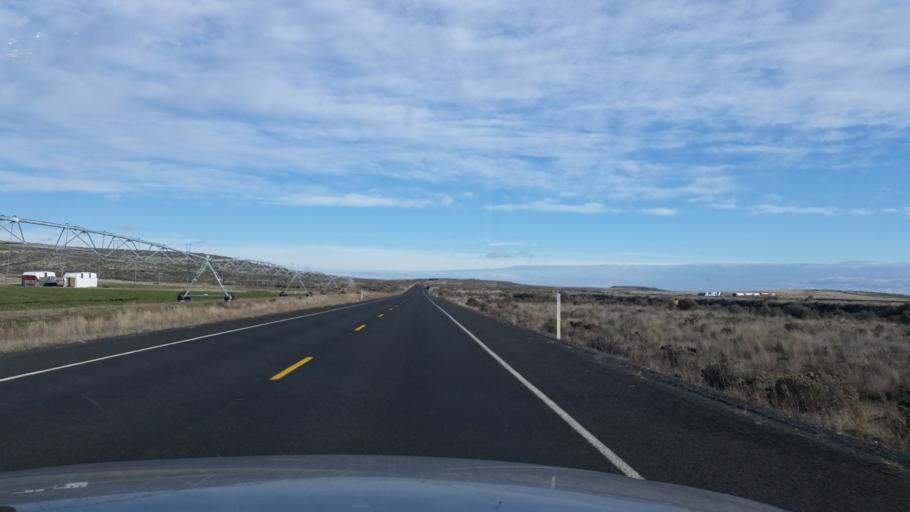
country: US
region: Washington
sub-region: Adams County
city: Ritzville
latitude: 47.3386
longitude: -118.6326
